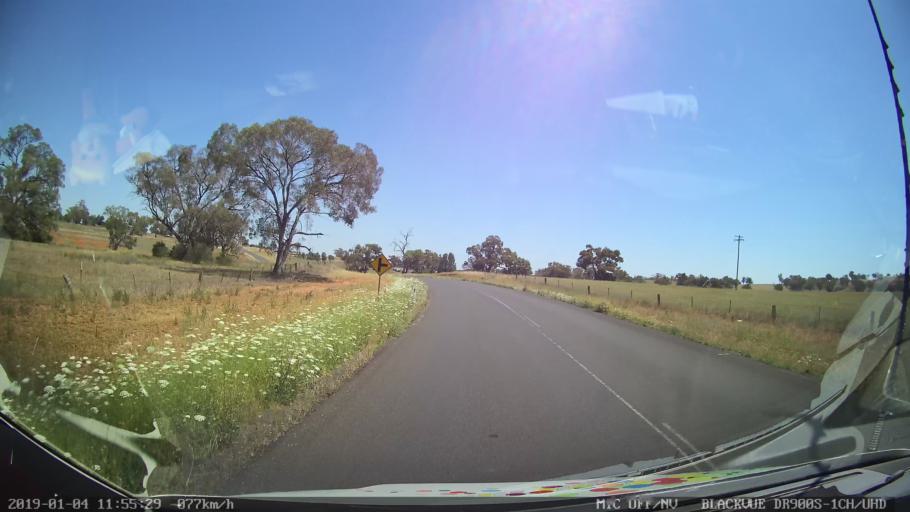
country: AU
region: New South Wales
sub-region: Cabonne
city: Molong
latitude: -32.8535
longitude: 148.7236
